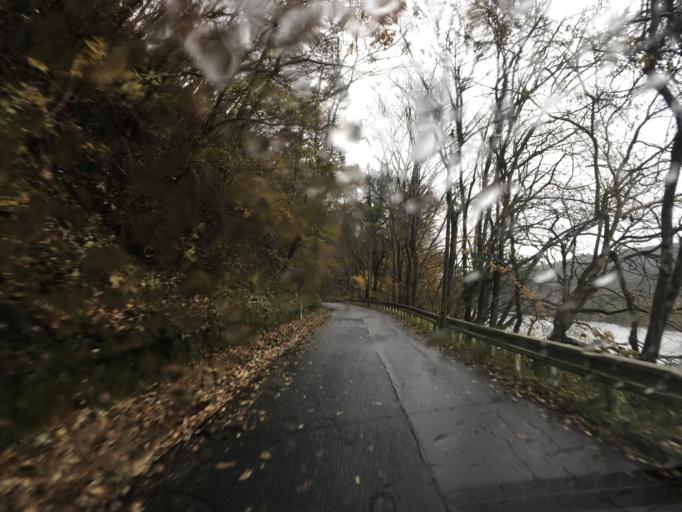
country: JP
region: Iwate
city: Ichinoseki
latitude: 38.8141
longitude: 141.2527
